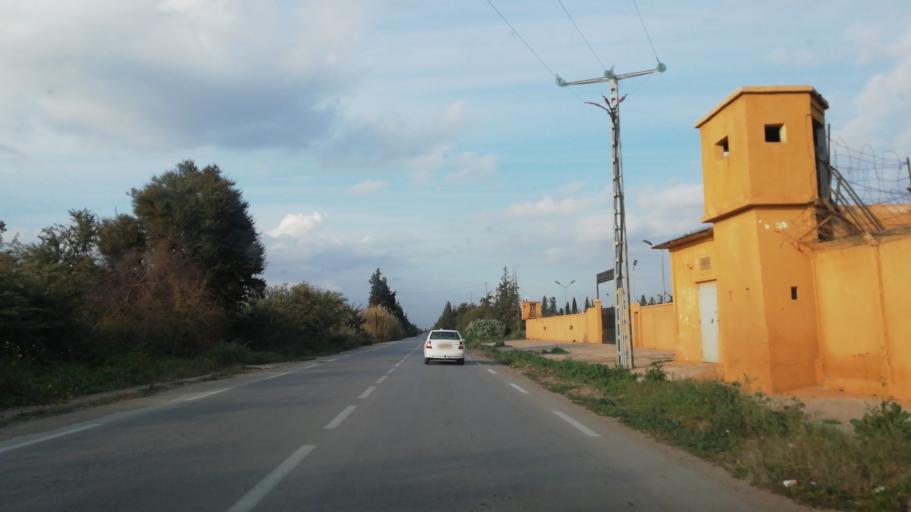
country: DZ
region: Mascara
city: Mascara
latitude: 35.6025
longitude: 0.0527
